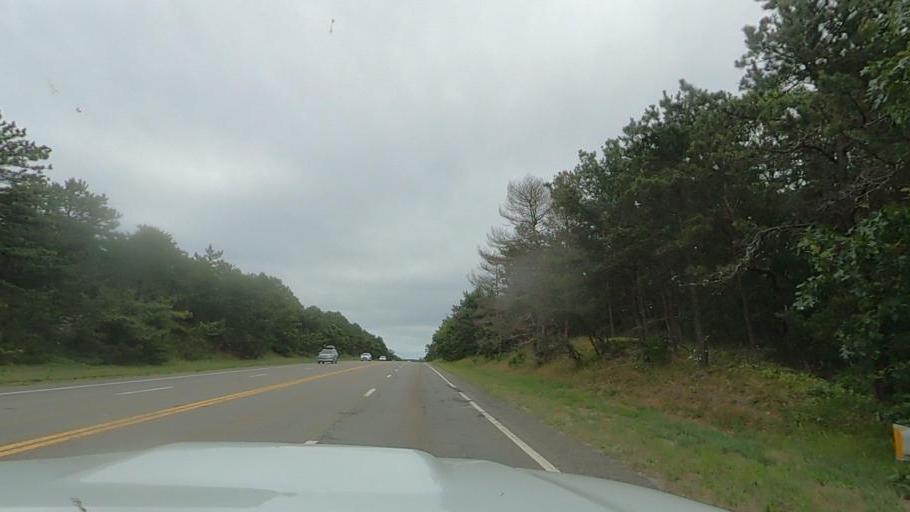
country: US
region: Massachusetts
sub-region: Barnstable County
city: Truro
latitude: 42.0426
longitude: -70.0922
